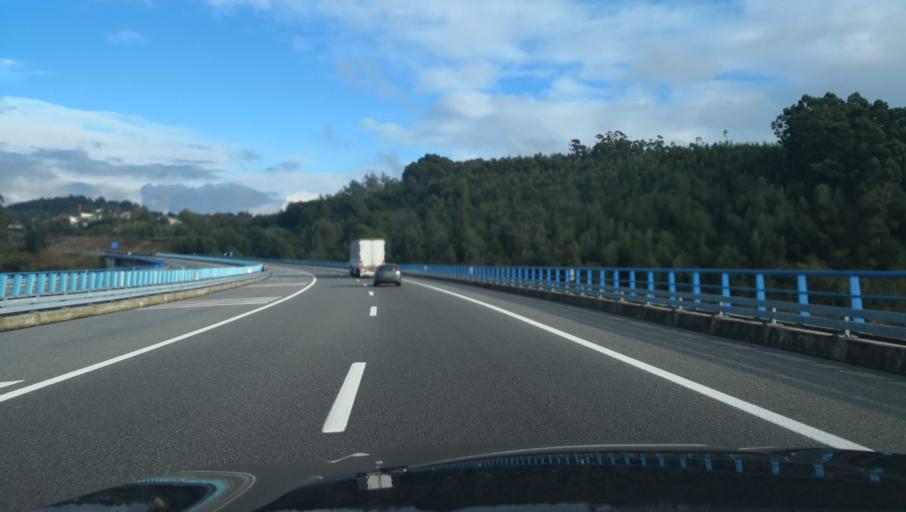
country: PT
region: Braga
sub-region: Guimaraes
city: Candoso
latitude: 41.4089
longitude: -8.3205
